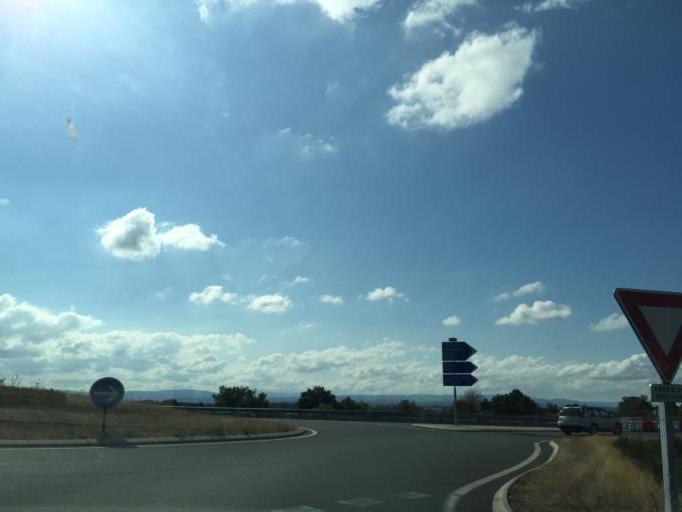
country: FR
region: Rhone-Alpes
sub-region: Departement de la Loire
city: Balbigny
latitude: 45.8436
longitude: 4.1630
